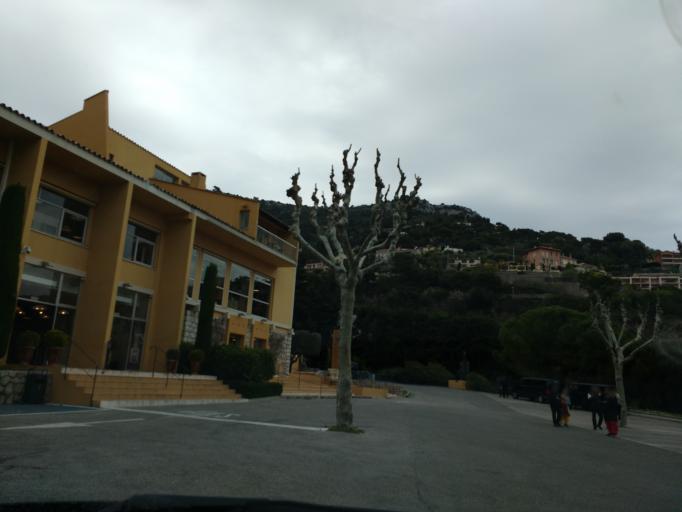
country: FR
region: Provence-Alpes-Cote d'Azur
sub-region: Departement des Alpes-Maritimes
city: Eze
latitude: 43.7295
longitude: 7.3635
